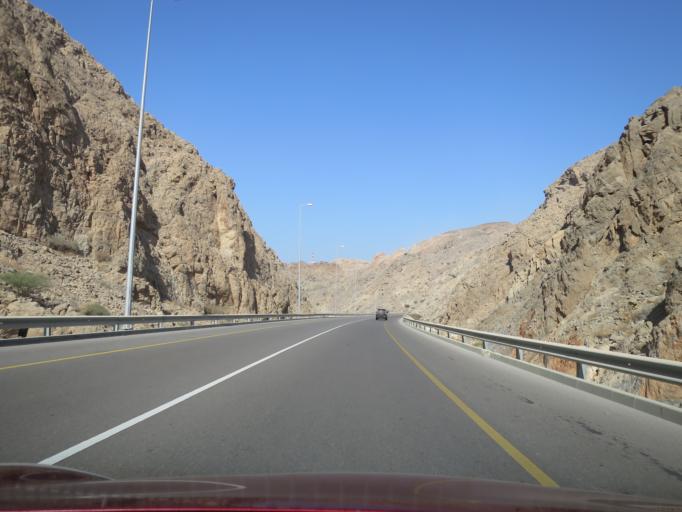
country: OM
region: Muhafazat Masqat
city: Muscat
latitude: 23.5287
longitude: 58.6457
